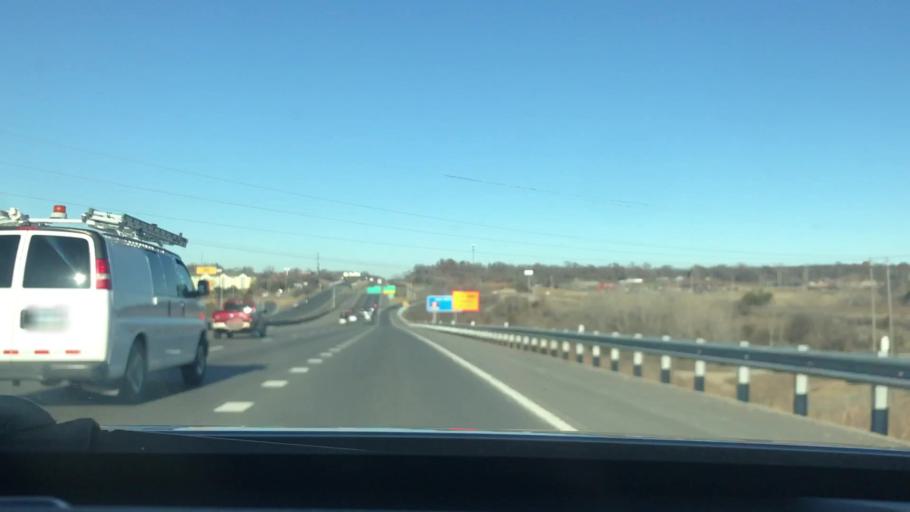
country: US
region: Missouri
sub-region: Jackson County
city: Raytown
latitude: 38.9628
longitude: -94.5228
